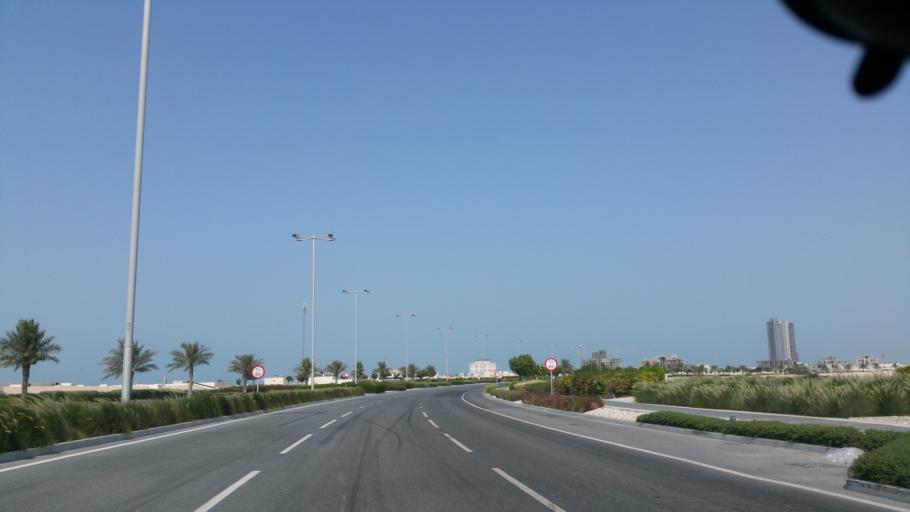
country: QA
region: Baladiyat Umm Salal
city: Umm Salal Muhammad
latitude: 25.4409
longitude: 51.5078
